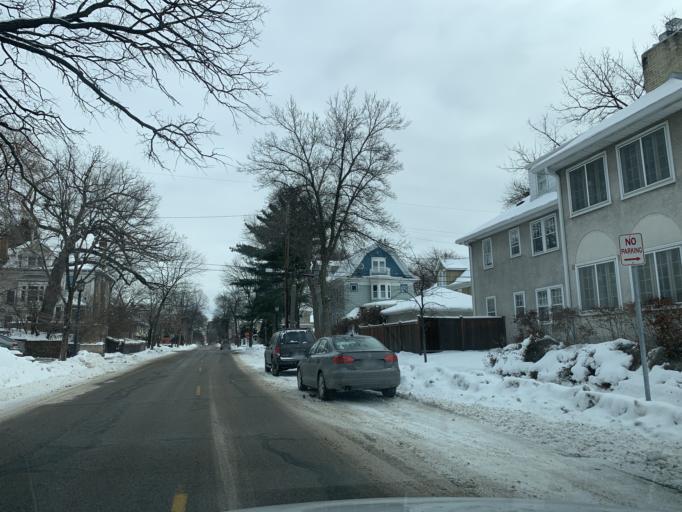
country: US
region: Minnesota
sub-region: Hennepin County
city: Minneapolis
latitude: 44.9664
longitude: -93.3007
